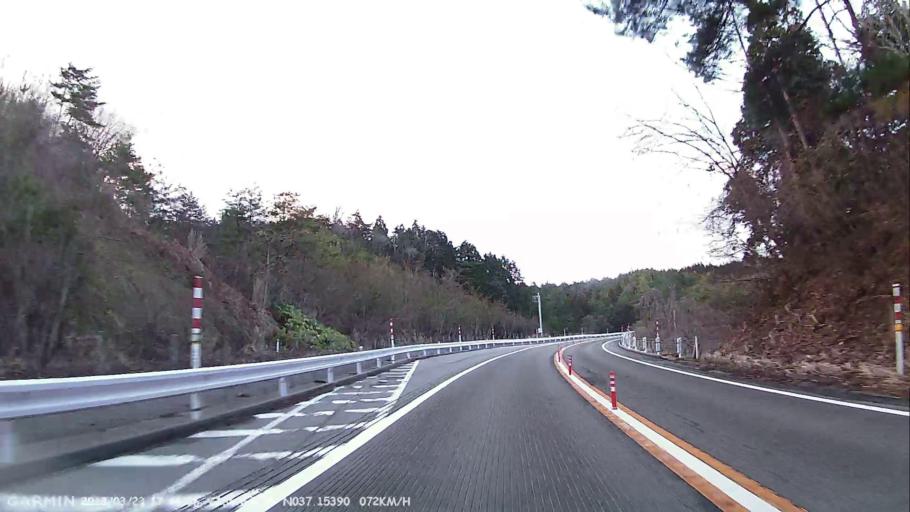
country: JP
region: Ishikawa
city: Nanao
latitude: 37.1541
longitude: 136.8457
